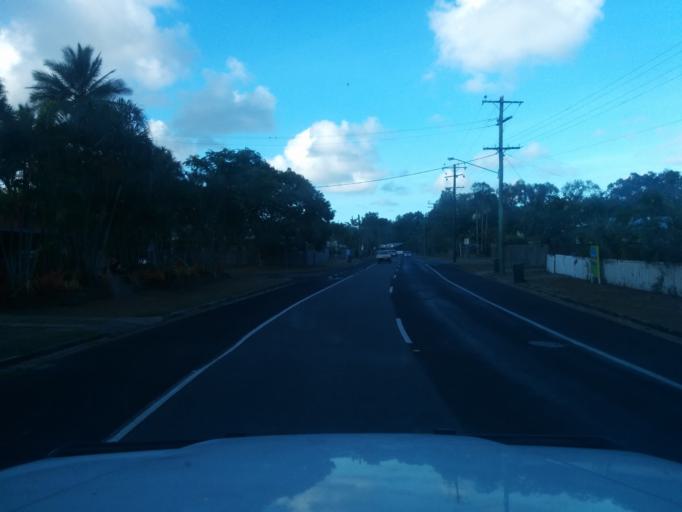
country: AU
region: Queensland
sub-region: Cairns
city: Cairns
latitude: -16.9200
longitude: 145.7467
